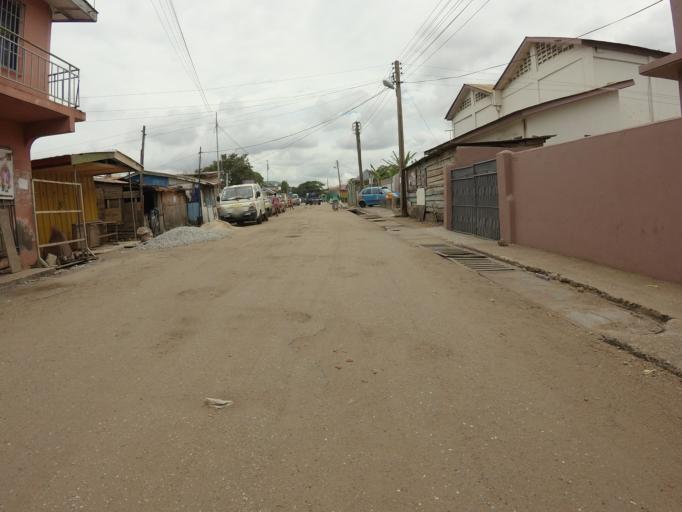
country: GH
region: Greater Accra
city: Accra
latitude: 5.5952
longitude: -0.2153
